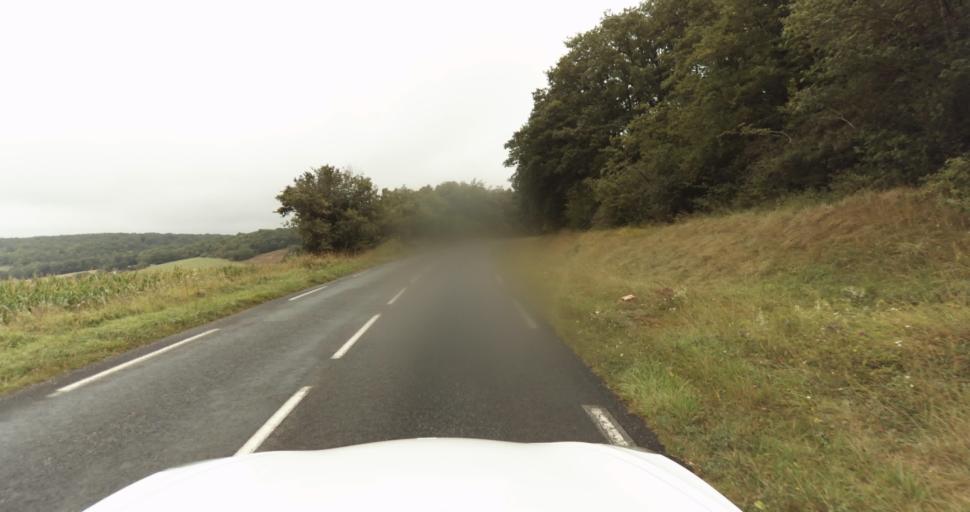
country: FR
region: Haute-Normandie
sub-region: Departement de l'Eure
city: Normanville
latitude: 49.0766
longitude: 1.1709
